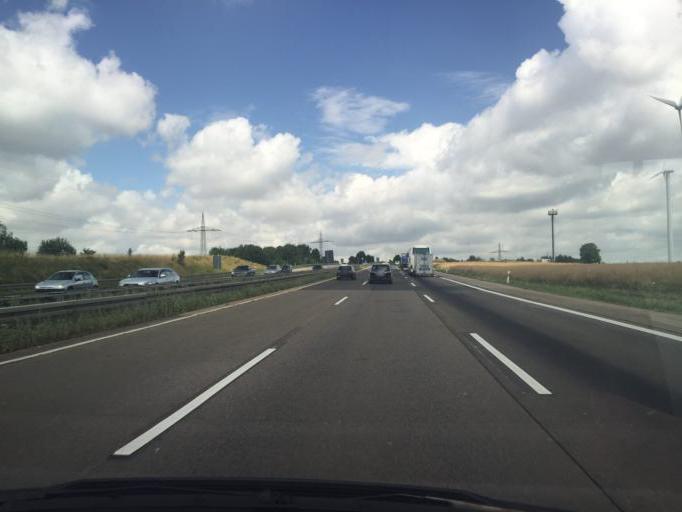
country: DE
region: Hesse
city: Bad Camberg
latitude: 50.2756
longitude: 8.2438
